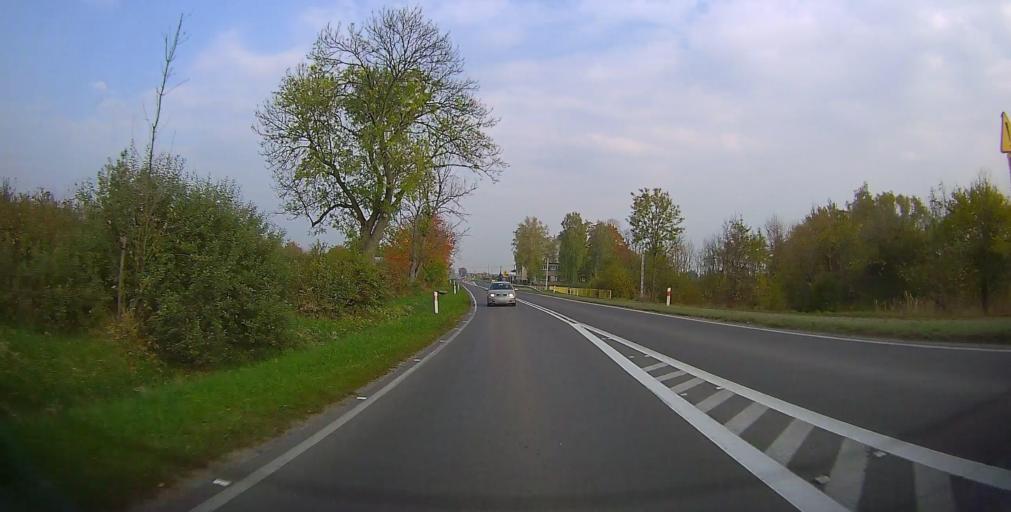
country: PL
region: Masovian Voivodeship
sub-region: Powiat grojecki
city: Mogielnica
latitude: 51.7448
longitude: 20.7628
